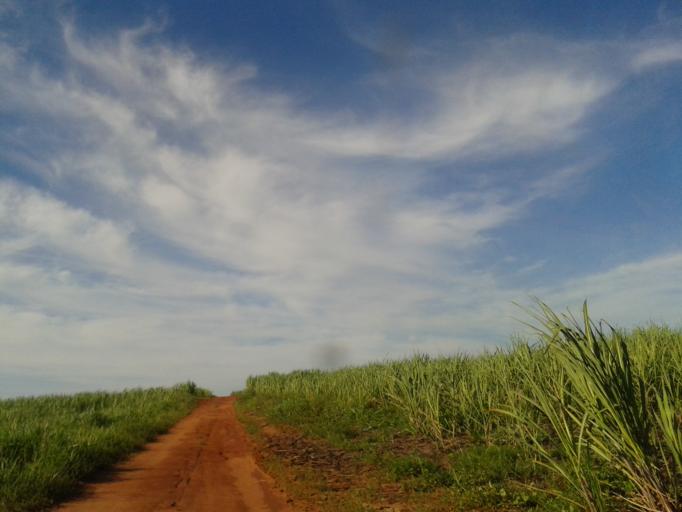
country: BR
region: Minas Gerais
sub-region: Santa Vitoria
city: Santa Vitoria
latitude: -19.1244
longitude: -50.0042
